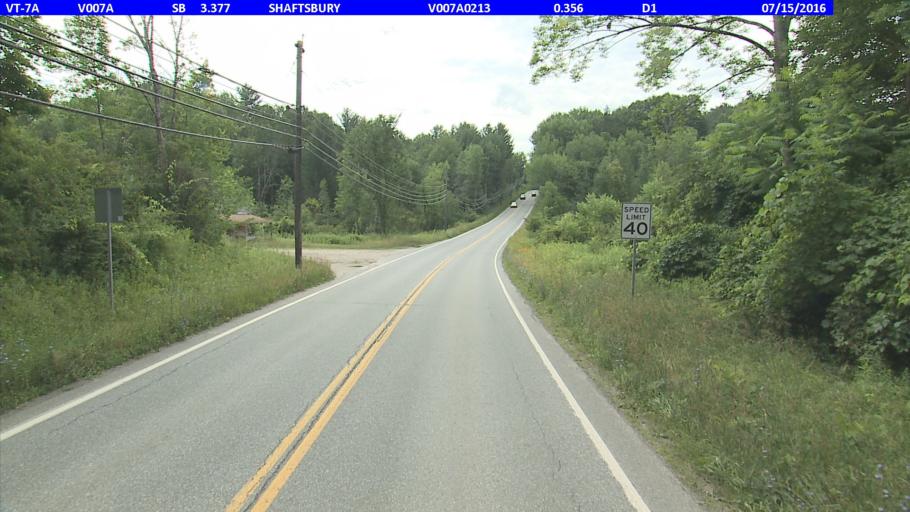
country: US
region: Vermont
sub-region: Bennington County
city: North Bennington
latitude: 42.9379
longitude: -73.2101
